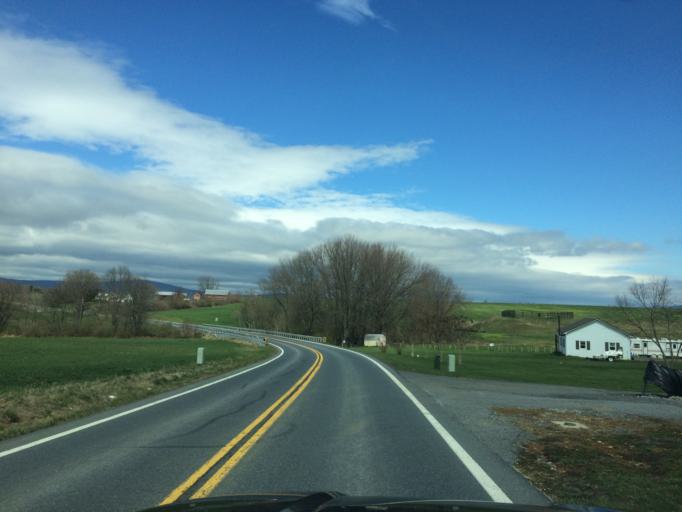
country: US
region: Maryland
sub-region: Frederick County
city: Jefferson
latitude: 39.3627
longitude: -77.5473
